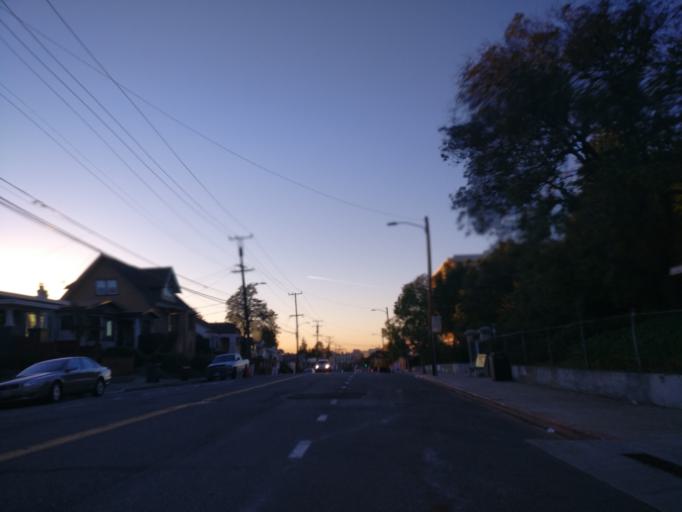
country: US
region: California
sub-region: Alameda County
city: Piedmont
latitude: 37.8001
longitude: -122.2210
